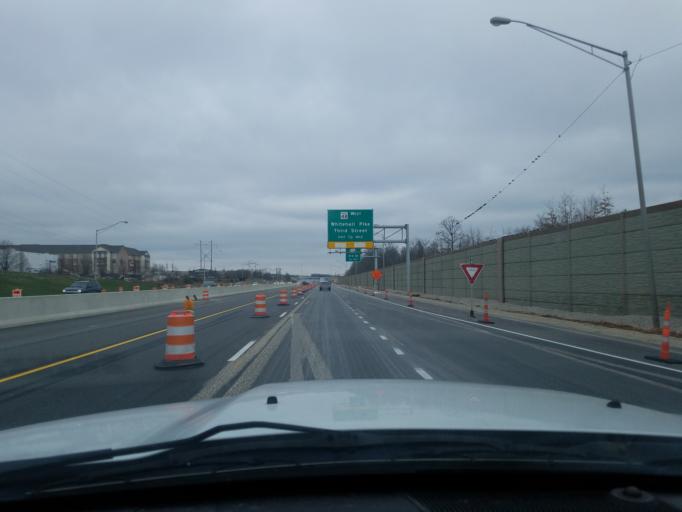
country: US
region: Indiana
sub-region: Monroe County
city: Bloomington
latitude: 39.1535
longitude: -86.5729
